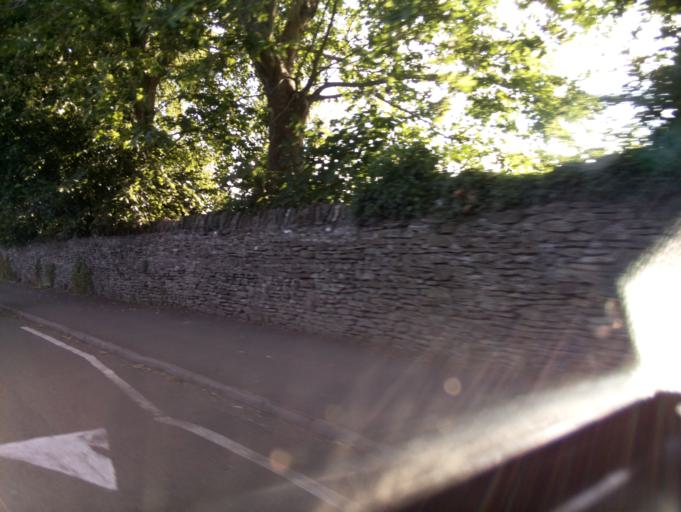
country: GB
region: England
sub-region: South Gloucestershire
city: Mangotsfield
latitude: 51.4809
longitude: -2.4847
